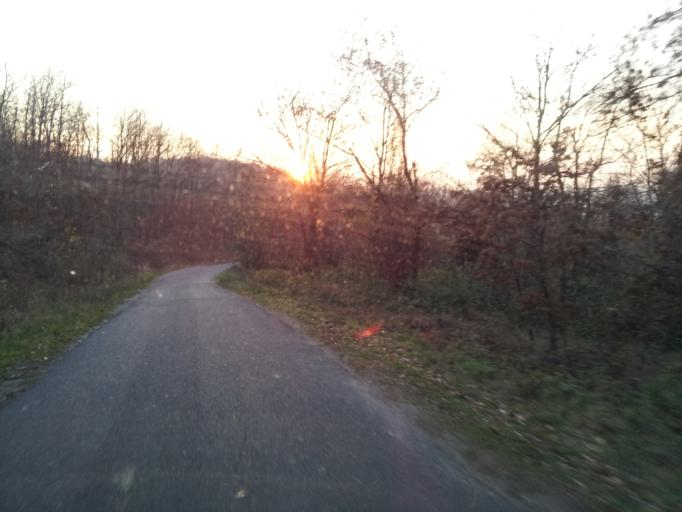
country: HU
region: Zala
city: Cserszegtomaj
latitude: 46.8462
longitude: 17.2101
